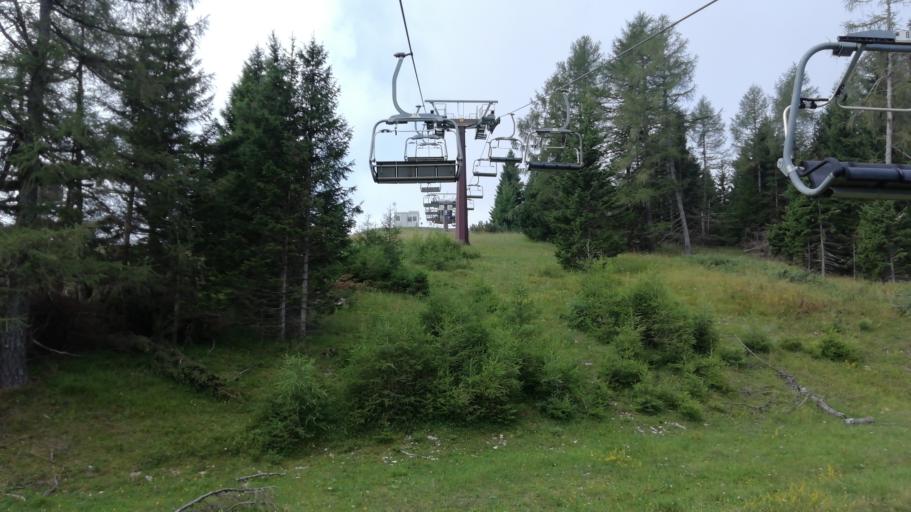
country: IT
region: Trentino-Alto Adige
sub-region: Provincia di Trento
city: Piazza
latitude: 45.8882
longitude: 11.1804
